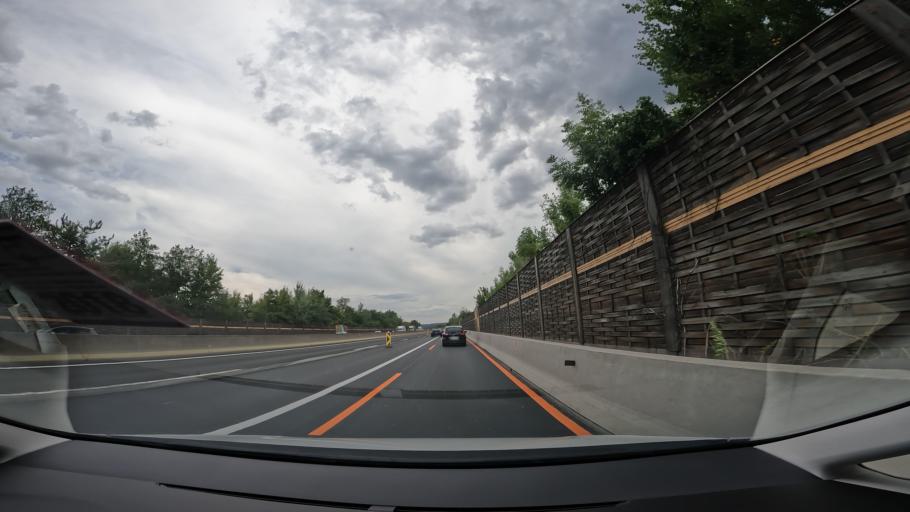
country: AT
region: Styria
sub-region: Politischer Bezirk Hartberg-Fuerstenfeld
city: Sankt Johann in der Haide
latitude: 47.2401
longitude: 15.9954
